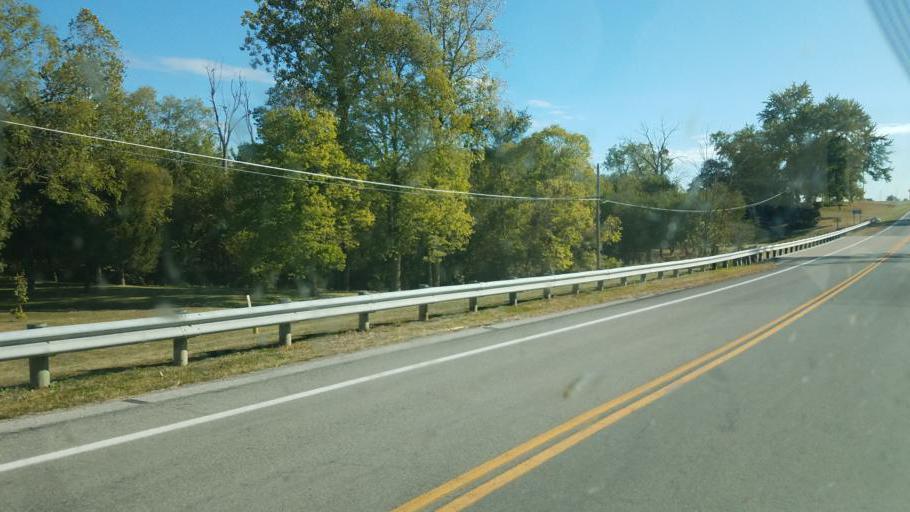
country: US
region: Ohio
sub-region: Wyandot County
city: Upper Sandusky
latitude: 40.7385
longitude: -83.2146
